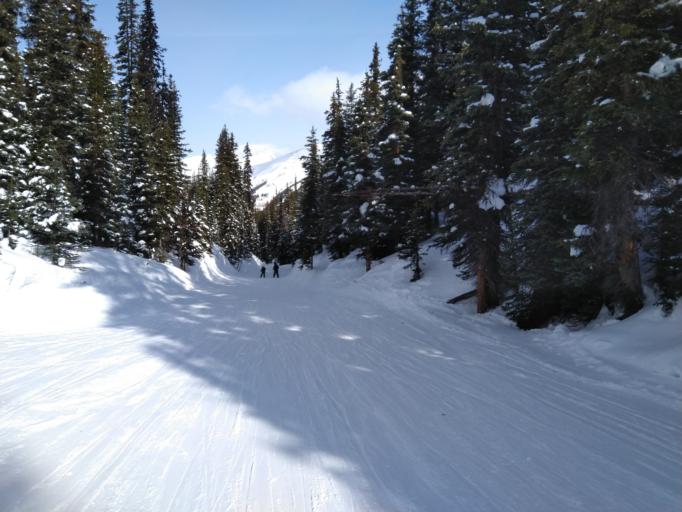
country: CA
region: Alberta
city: Banff
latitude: 51.0904
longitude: -115.7686
